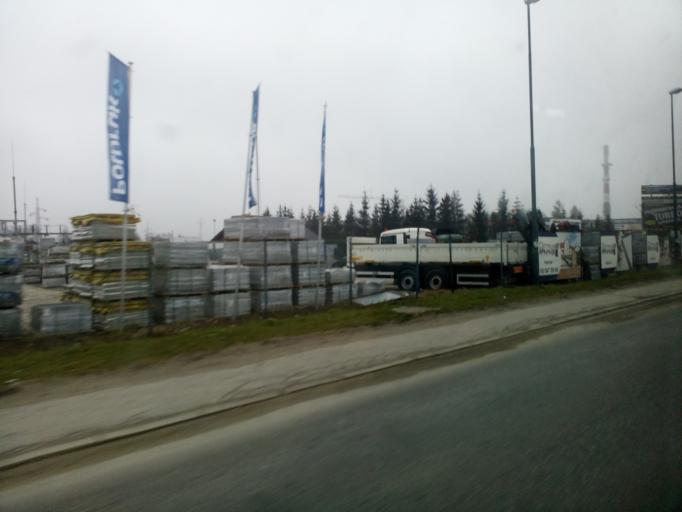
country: PL
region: Lesser Poland Voivodeship
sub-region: Powiat nowosadecki
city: Nowy Sacz
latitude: 49.5895
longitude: 20.6759
